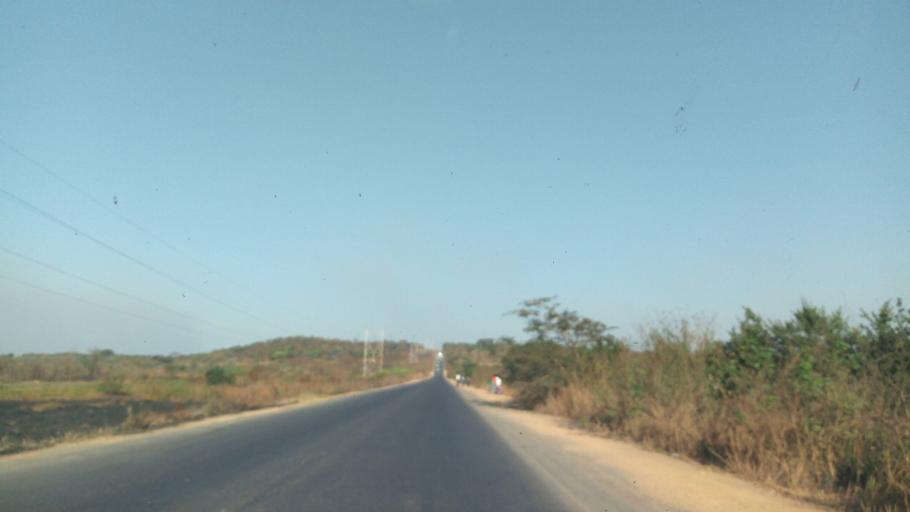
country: CD
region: Katanga
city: Likasi
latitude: -11.0528
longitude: 26.9607
